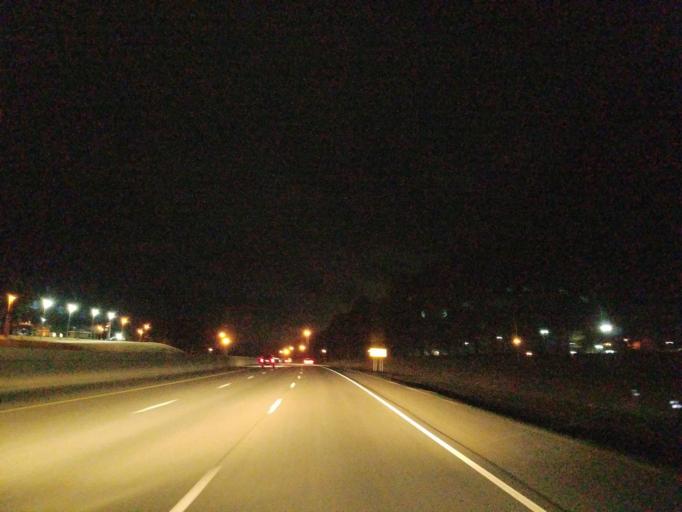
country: US
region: Alabama
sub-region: Tuscaloosa County
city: Coaling
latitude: 33.1902
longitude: -87.3230
